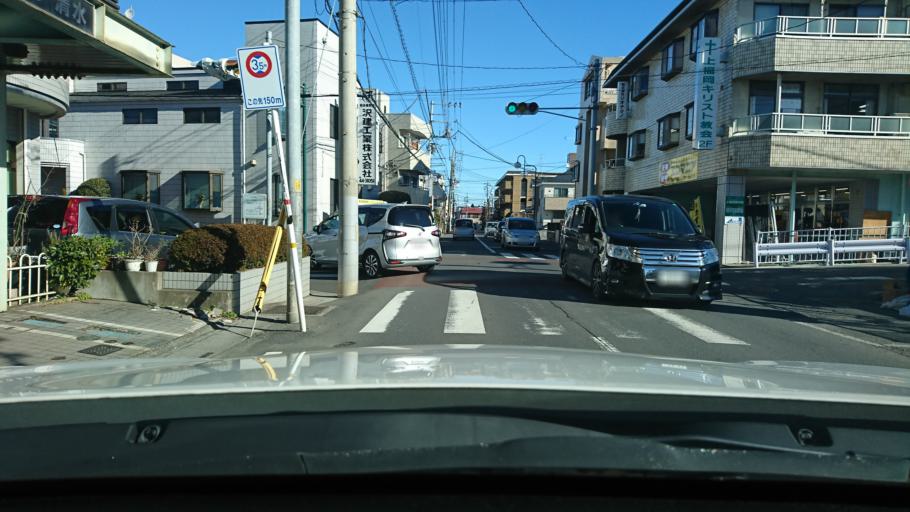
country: JP
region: Saitama
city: Kamifukuoka
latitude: 35.8770
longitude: 139.5062
